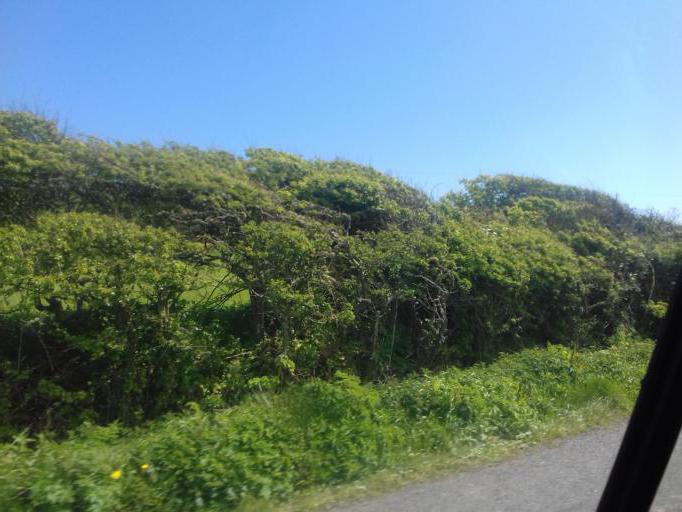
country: IE
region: Munster
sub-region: Waterford
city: Dunmore East
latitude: 52.1751
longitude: -6.8961
